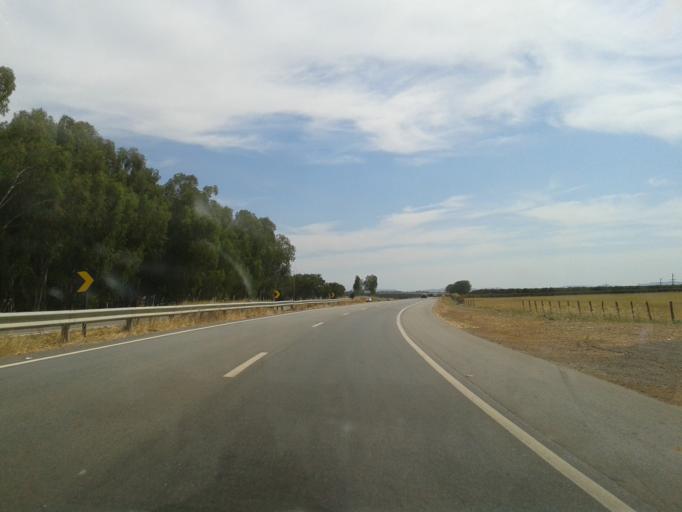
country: BR
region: Goias
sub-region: Itaberai
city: Itaberai
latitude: -16.0751
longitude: -49.7515
